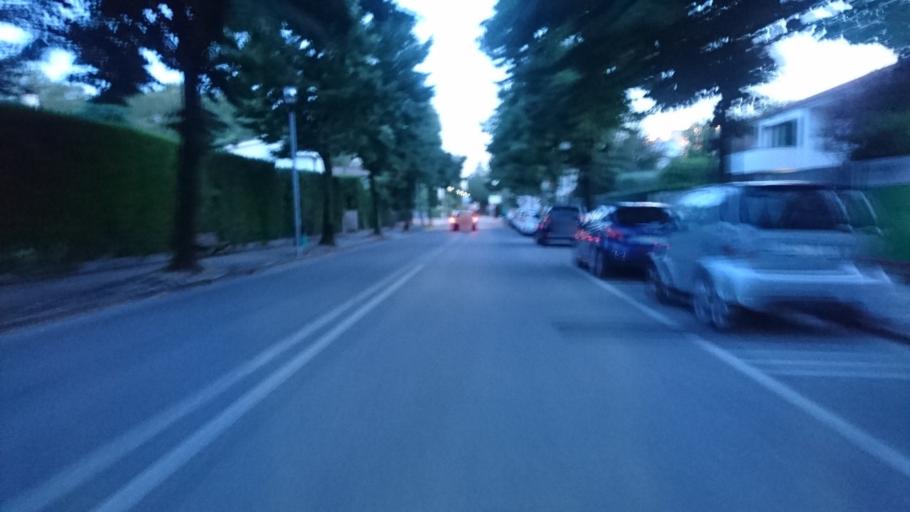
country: IT
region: Veneto
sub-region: Provincia di Padova
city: Abano Terme
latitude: 45.3549
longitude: 11.7788
